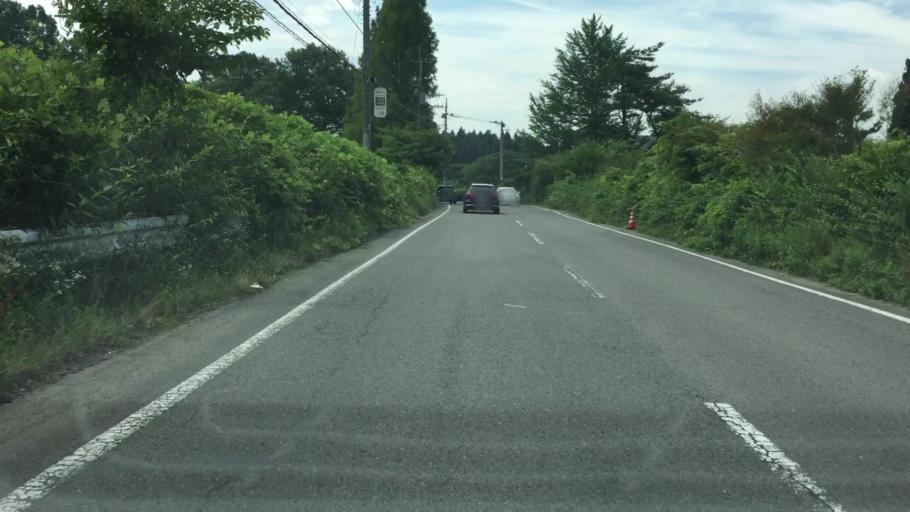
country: JP
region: Tochigi
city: Kuroiso
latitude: 37.0441
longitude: 140.0434
